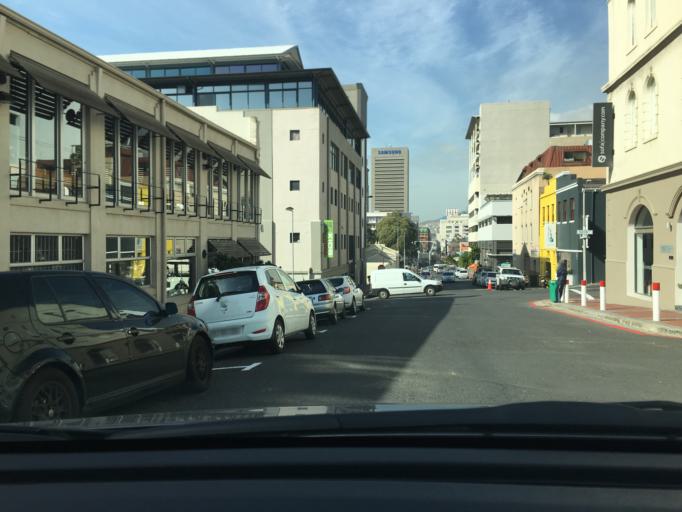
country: ZA
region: Western Cape
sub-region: City of Cape Town
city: Cape Town
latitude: -33.9167
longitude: 18.4176
